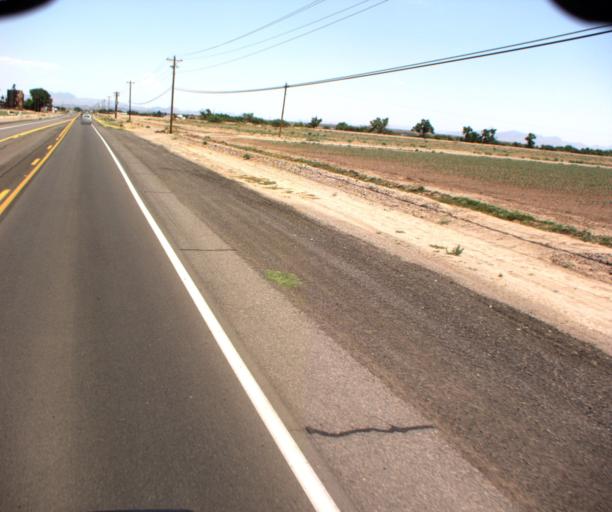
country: US
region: Arizona
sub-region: Graham County
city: Safford
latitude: 32.8166
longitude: -109.6531
